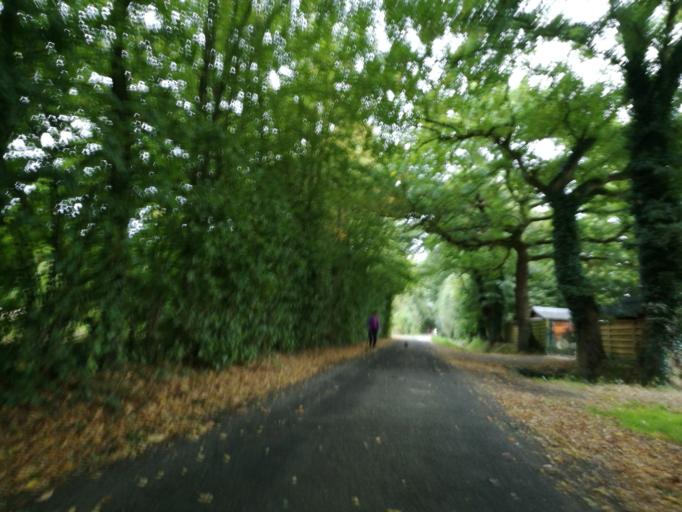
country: FR
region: Brittany
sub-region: Departement d'Ille-et-Vilaine
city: Bedee
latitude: 48.1697
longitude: -1.9466
